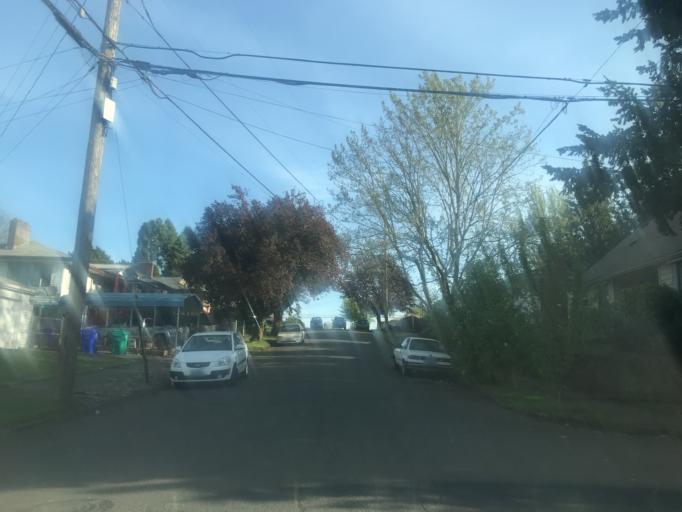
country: US
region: Oregon
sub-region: Multnomah County
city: Lents
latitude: 45.5019
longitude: -122.5819
